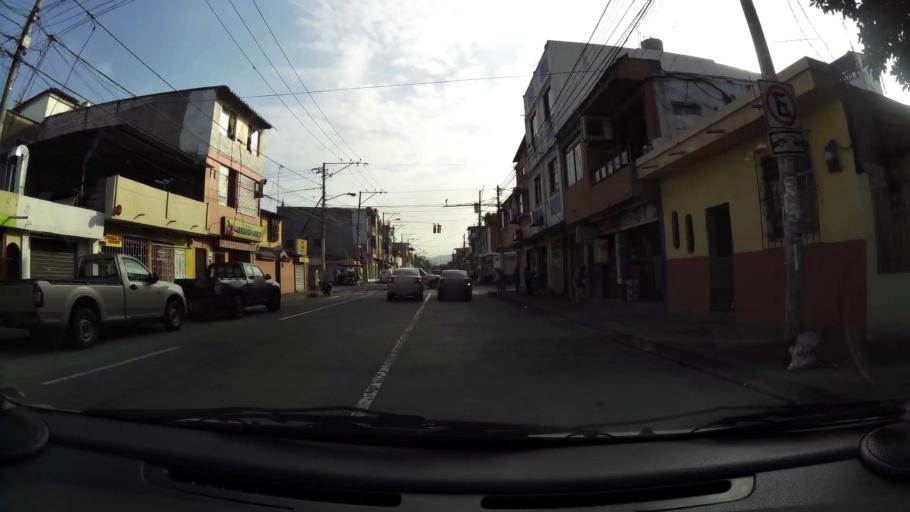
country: EC
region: Guayas
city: Eloy Alfaro
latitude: -2.1257
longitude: -79.8965
